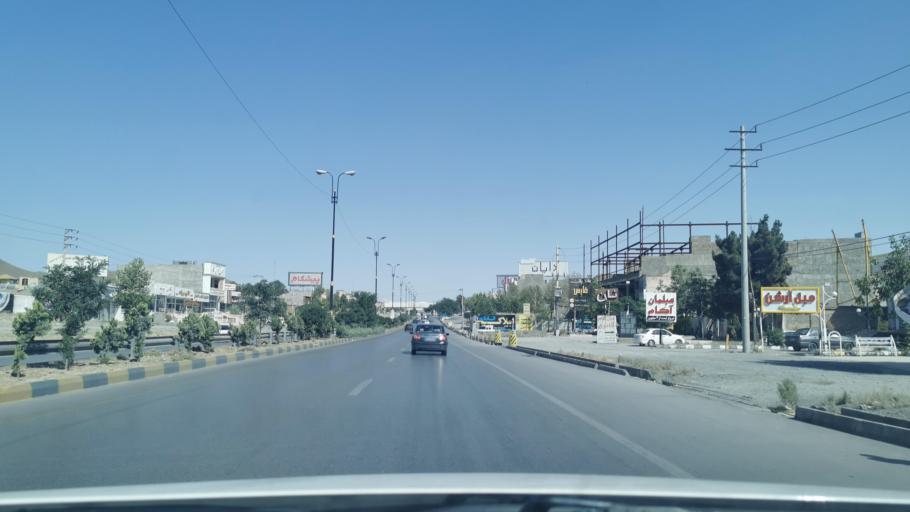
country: IR
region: Razavi Khorasan
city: Torqabeh
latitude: 36.3949
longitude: 59.3985
